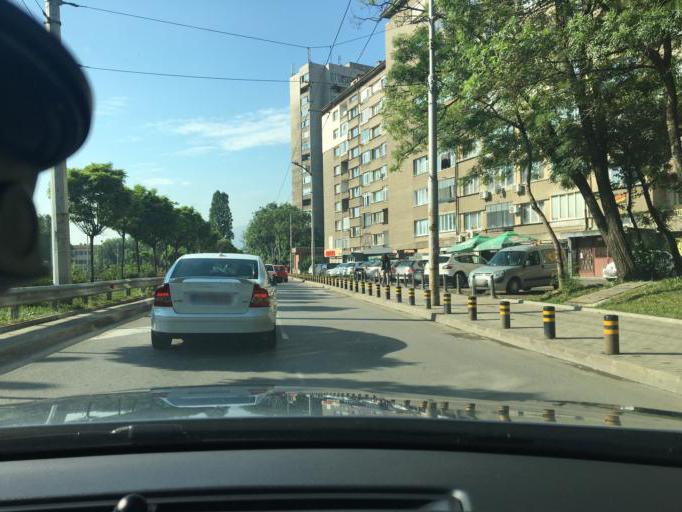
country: BG
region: Sofia-Capital
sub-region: Stolichna Obshtina
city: Sofia
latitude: 42.6835
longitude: 23.3011
